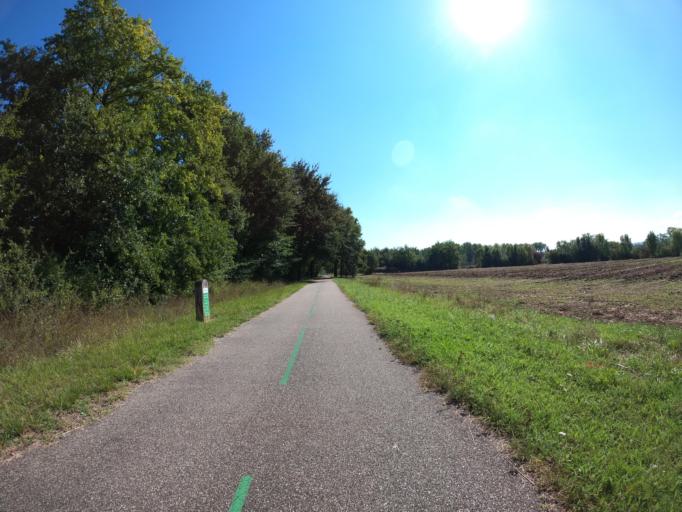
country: FR
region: Aquitaine
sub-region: Departement du Lot-et-Garonne
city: Bias
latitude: 44.4233
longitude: 0.6520
